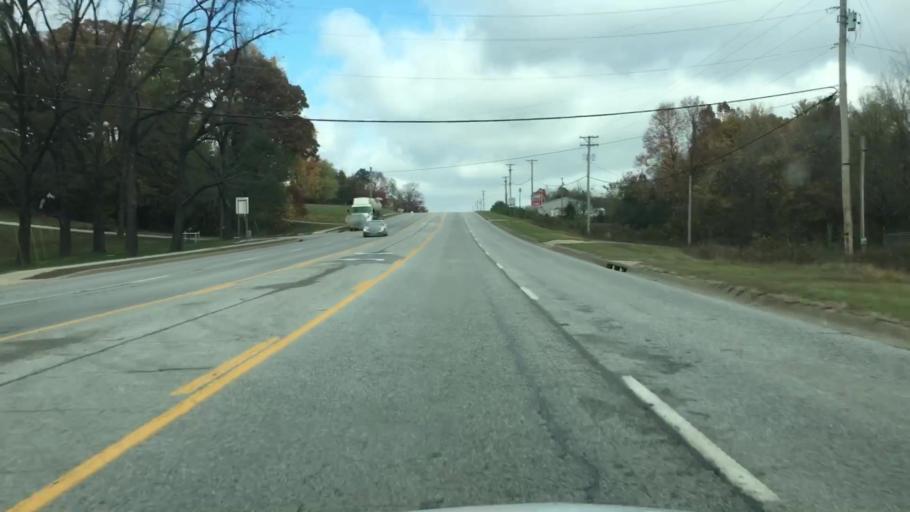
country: US
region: Arkansas
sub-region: Benton County
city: Gentry
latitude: 36.2528
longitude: -94.4853
